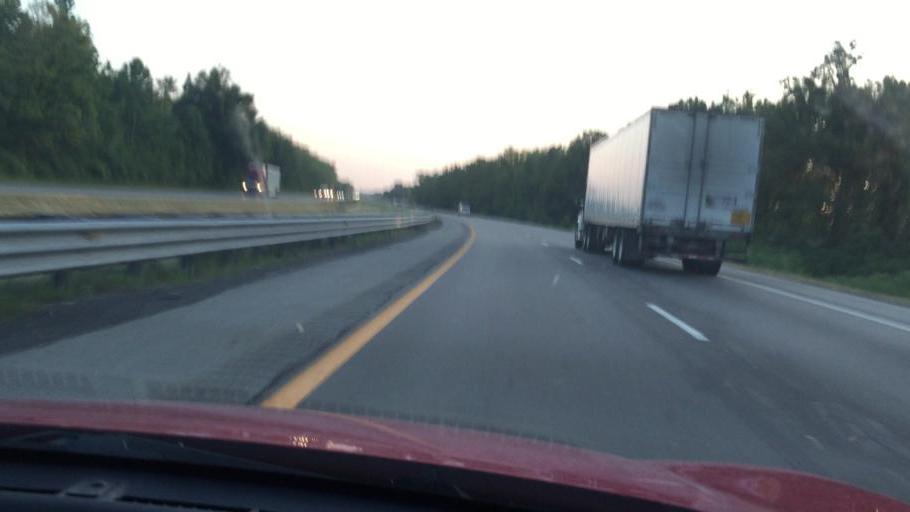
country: US
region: Michigan
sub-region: Washtenaw County
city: Milan
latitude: 42.0435
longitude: -83.6697
